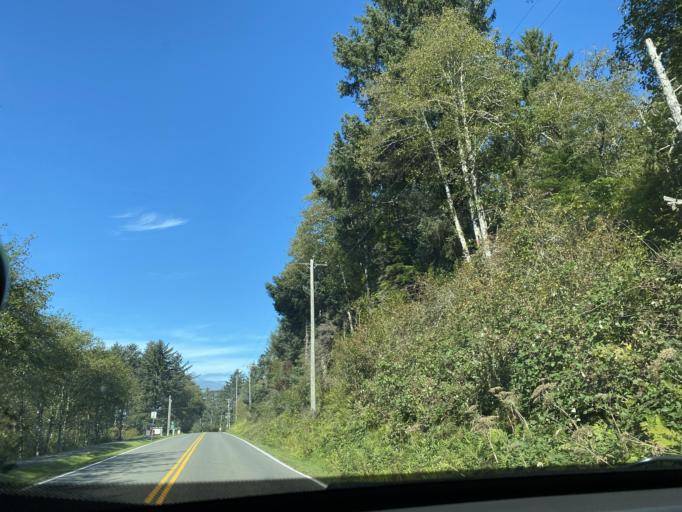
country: US
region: Washington
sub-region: Clallam County
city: Forks
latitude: 47.9030
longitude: -124.6283
